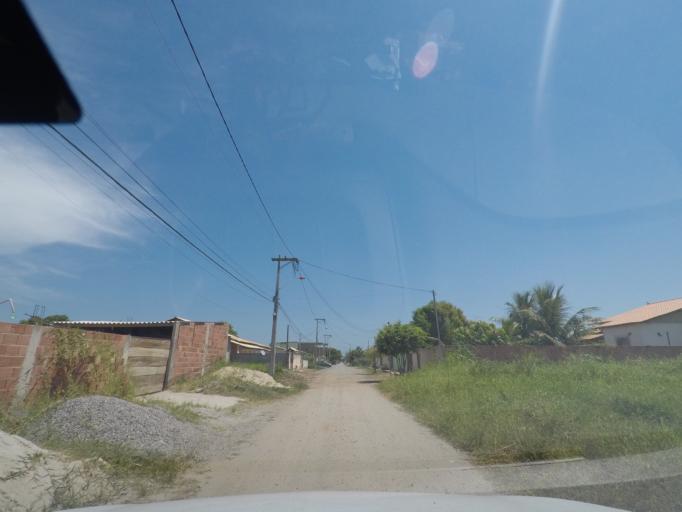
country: BR
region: Rio de Janeiro
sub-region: Marica
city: Marica
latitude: -22.9520
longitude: -42.9568
